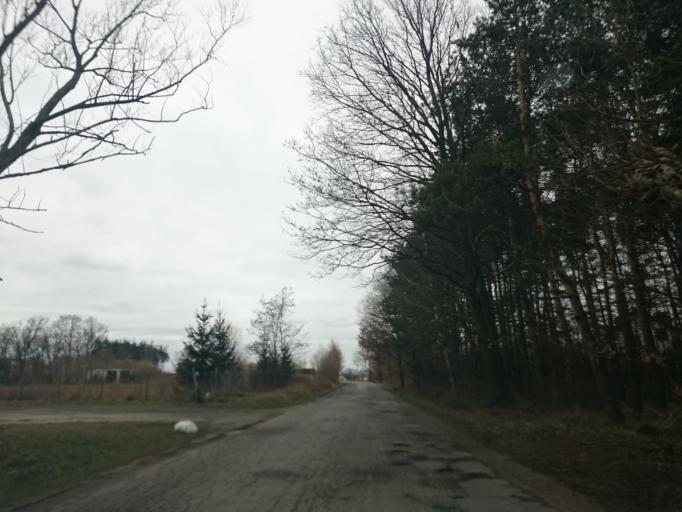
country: PL
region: Kujawsko-Pomorskie
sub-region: Powiat torunski
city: Lubicz Gorny
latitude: 53.0381
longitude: 18.7926
